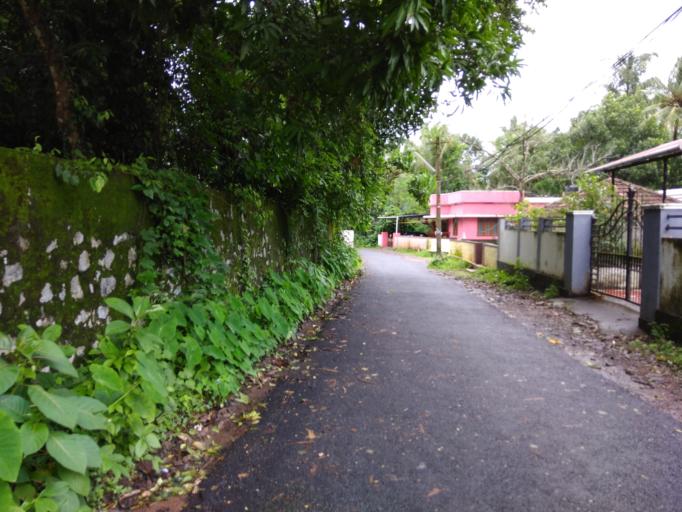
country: IN
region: Kerala
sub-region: Thrissur District
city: Avanoor
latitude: 10.5622
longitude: 76.1751
